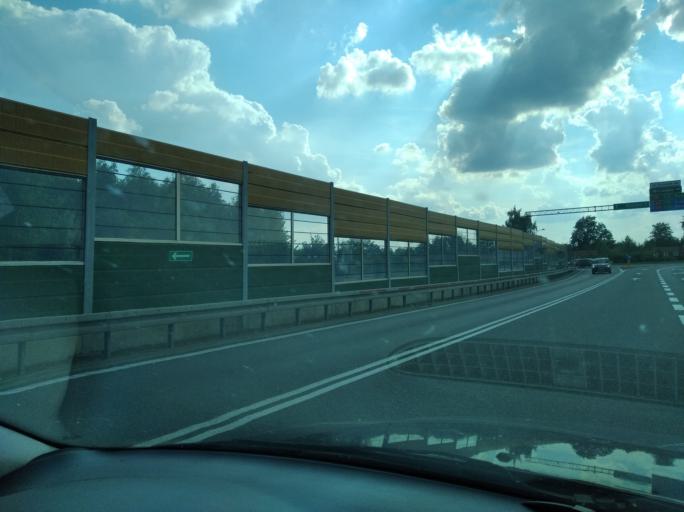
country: PL
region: Subcarpathian Voivodeship
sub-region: Powiat rzeszowski
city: Rudna Mala
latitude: 50.1065
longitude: 21.9777
